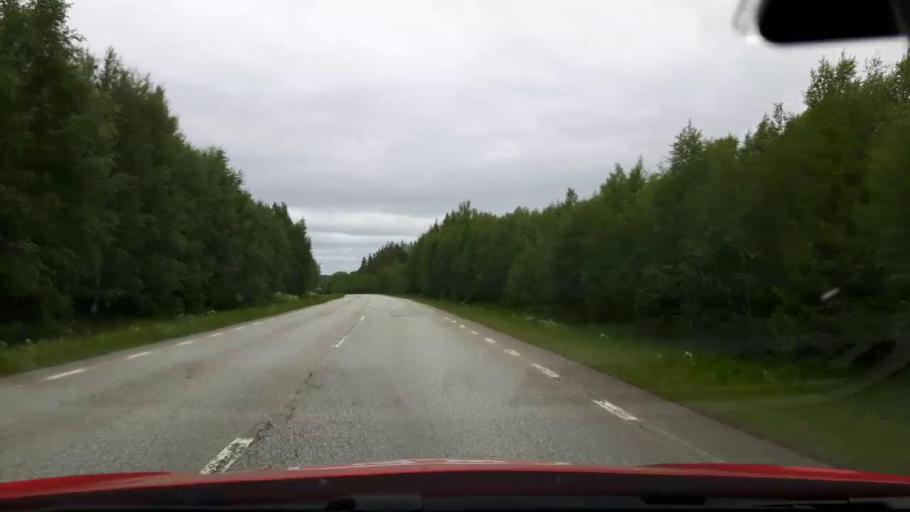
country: SE
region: Jaemtland
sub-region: OEstersunds Kommun
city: Lit
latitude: 63.6063
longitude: 14.6709
